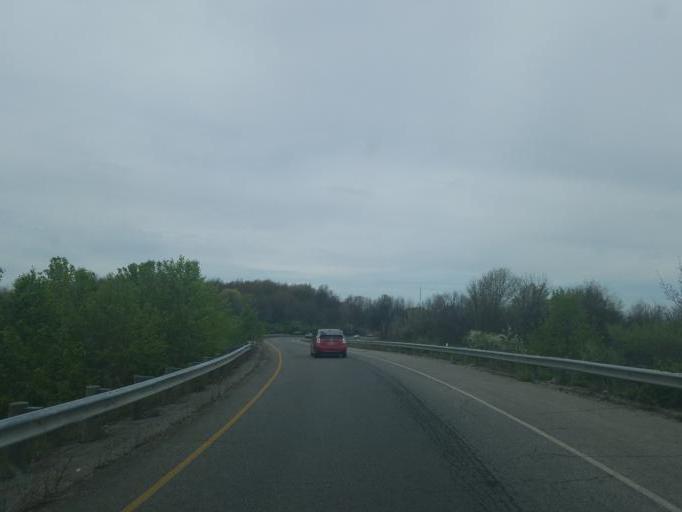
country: US
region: Ohio
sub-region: Summit County
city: Norton
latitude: 40.9950
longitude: -81.6605
